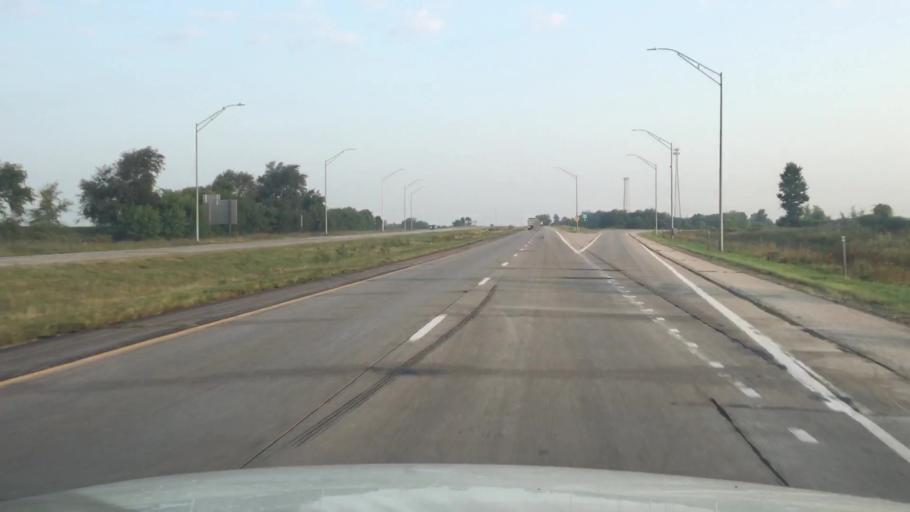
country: US
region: Iowa
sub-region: Polk County
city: Altoona
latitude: 41.6547
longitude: -93.5177
